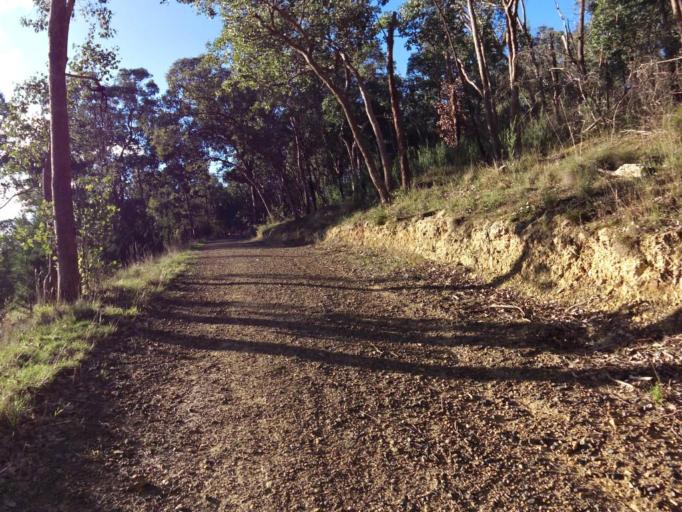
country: AU
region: Victoria
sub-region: Manningham
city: Warrandyte
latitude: -37.7350
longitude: 145.2315
